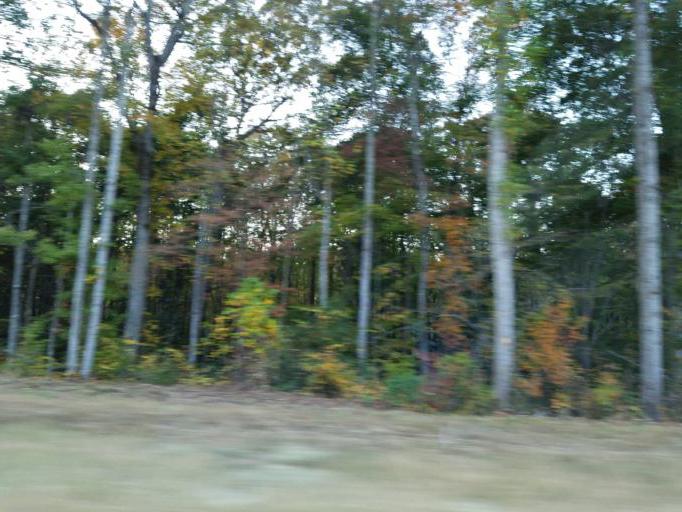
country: US
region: Georgia
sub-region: Lumpkin County
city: Dahlonega
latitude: 34.4483
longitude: -83.9851
